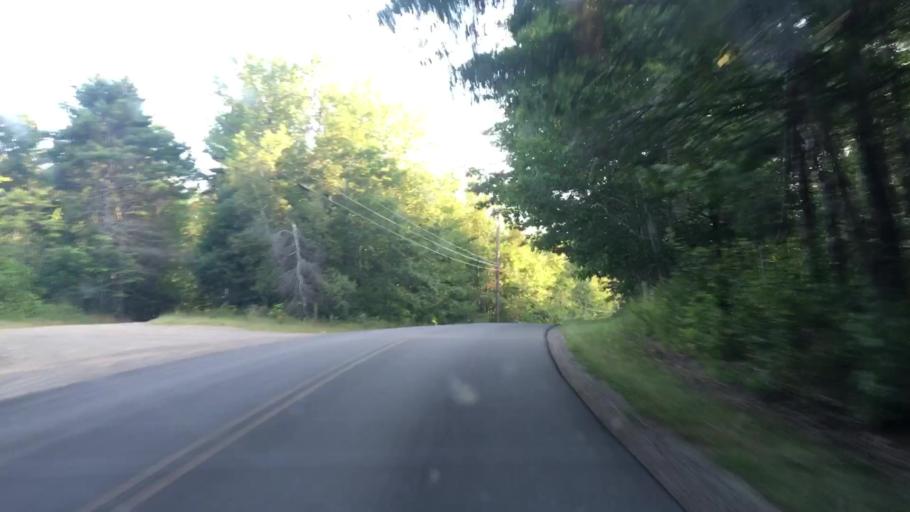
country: US
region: Maine
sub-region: Penobscot County
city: Hampden
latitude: 44.7058
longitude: -68.8888
